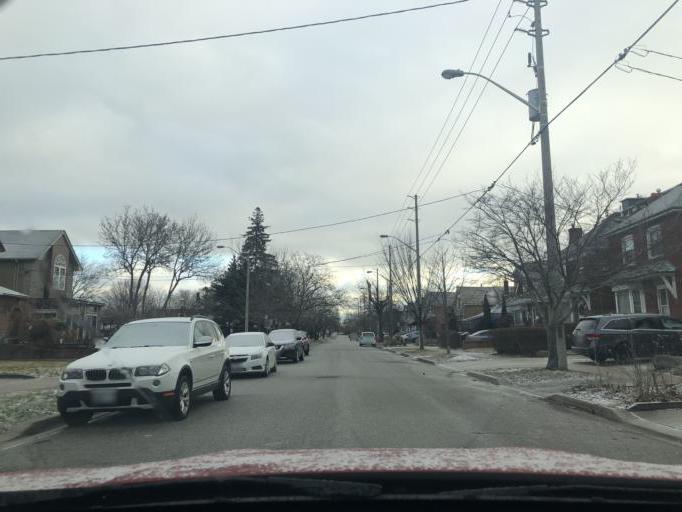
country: CA
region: Ontario
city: Toronto
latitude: 43.6906
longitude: -79.3478
